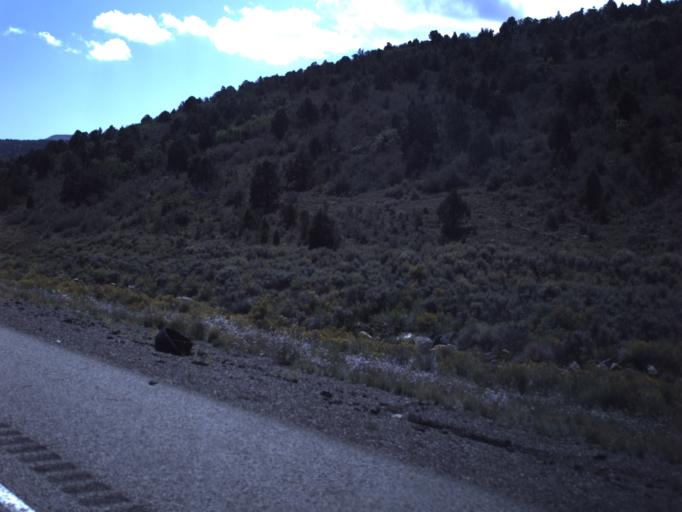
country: US
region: Utah
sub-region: Wayne County
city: Loa
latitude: 38.7744
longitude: -111.4760
